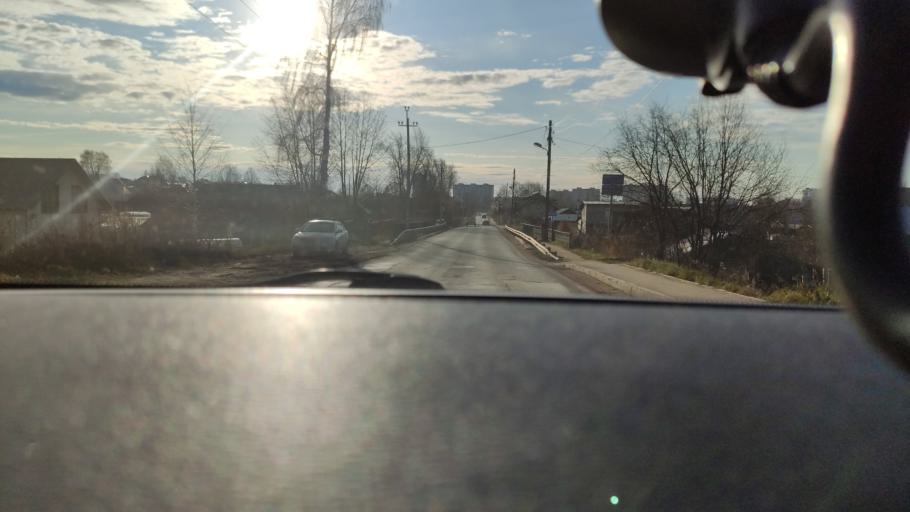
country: RU
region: Perm
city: Kondratovo
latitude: 58.0515
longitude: 56.0292
